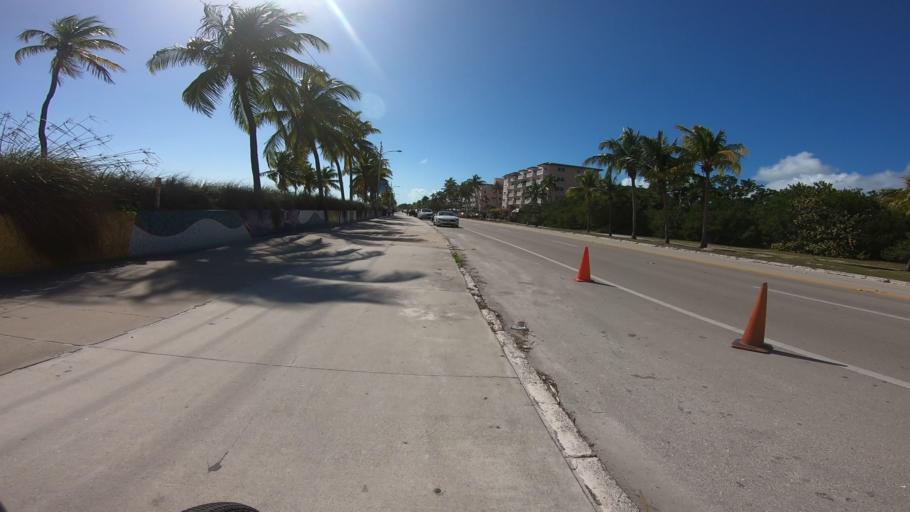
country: US
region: Florida
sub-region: Monroe County
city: Key West
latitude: 24.5519
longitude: -81.7692
